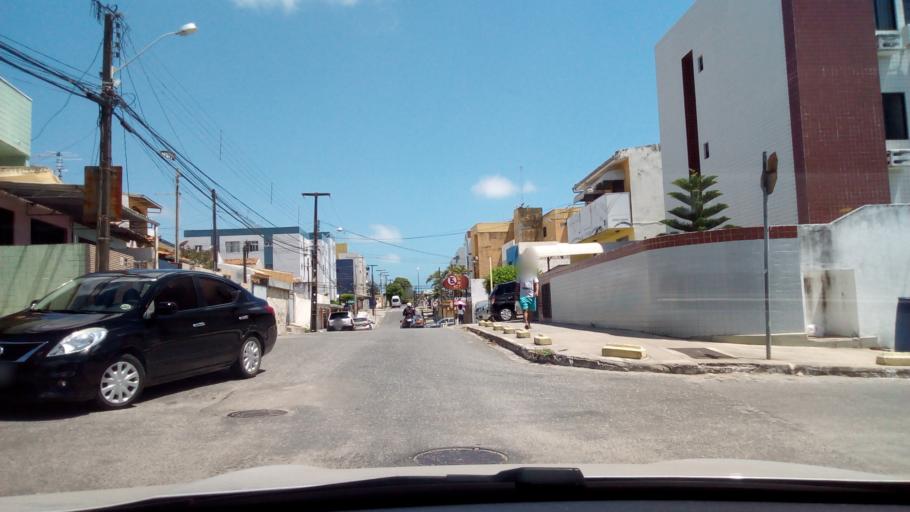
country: BR
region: Paraiba
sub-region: Joao Pessoa
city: Joao Pessoa
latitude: -7.1500
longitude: -34.8468
